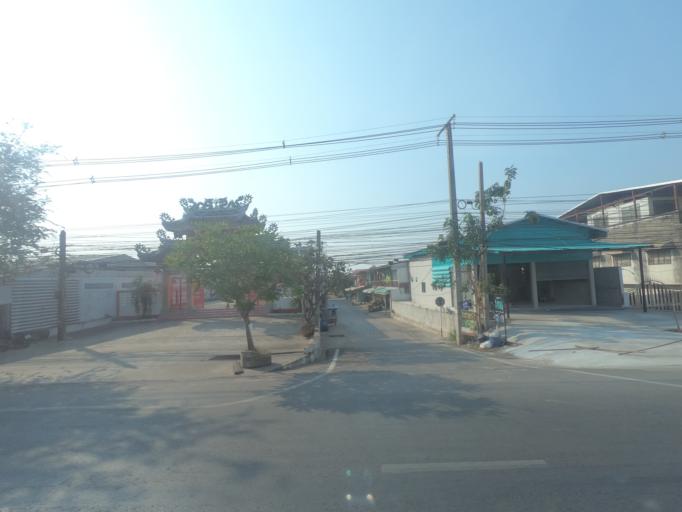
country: TH
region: Khon Kaen
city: Khon Kaen
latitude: 16.3403
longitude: 102.8017
